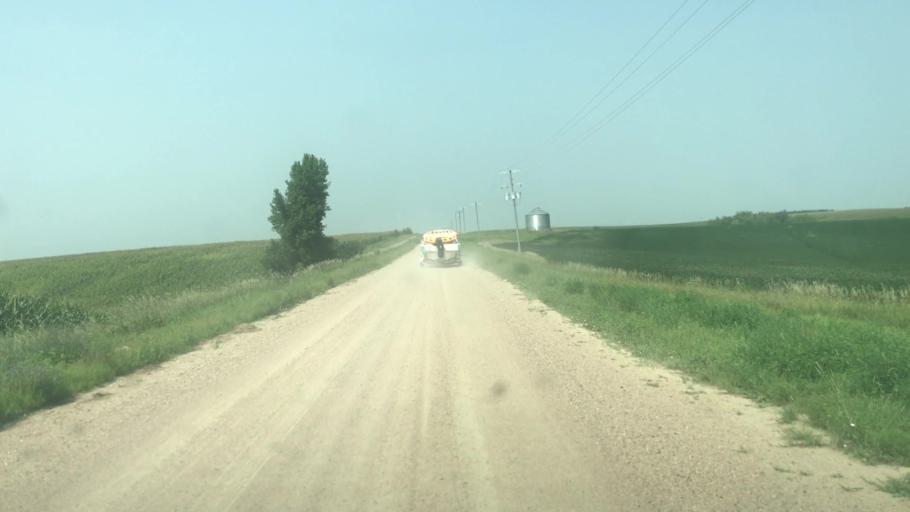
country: US
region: Nebraska
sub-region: Sherman County
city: Loup City
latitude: 41.2671
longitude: -98.9191
